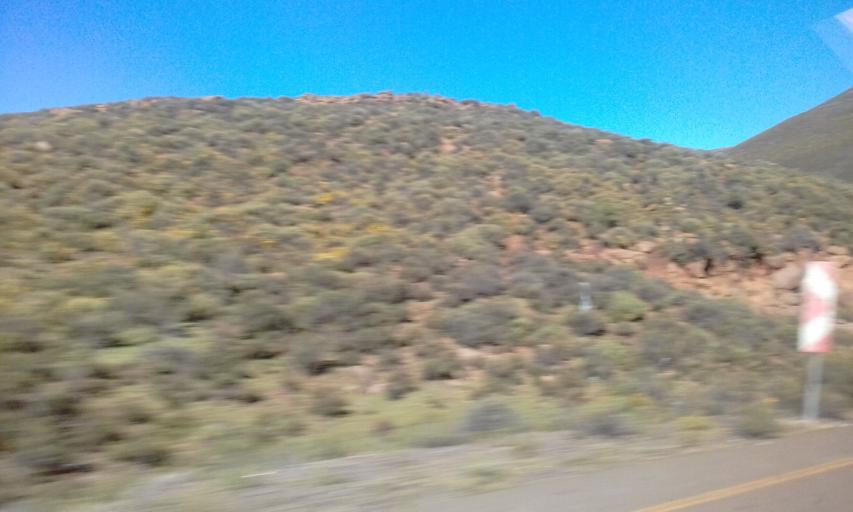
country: LS
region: Thaba-Tseka
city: Thaba-Tseka
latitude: -29.5095
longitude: 28.5096
